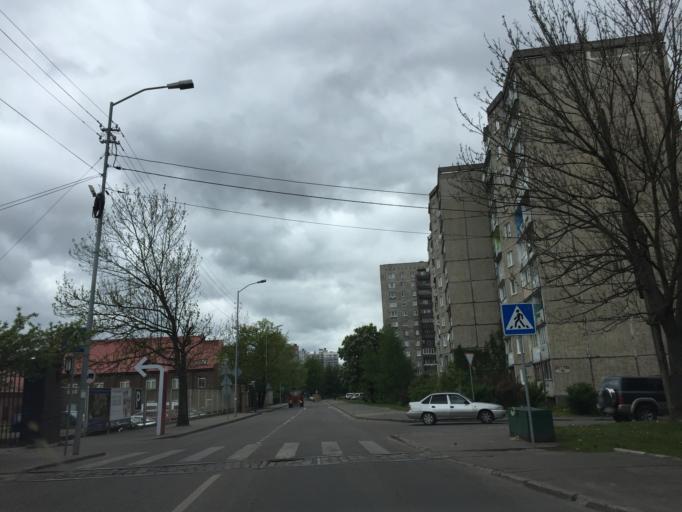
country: RU
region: Kaliningrad
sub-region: Gorod Kaliningrad
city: Kaliningrad
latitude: 54.7069
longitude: 20.4991
